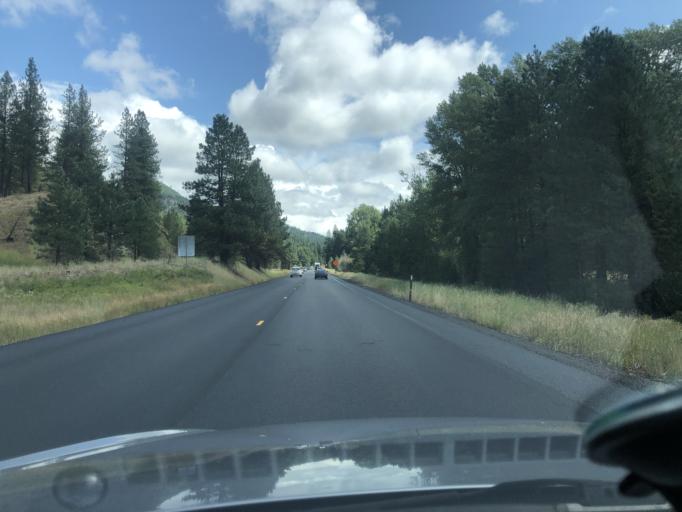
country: US
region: Washington
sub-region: Chelan County
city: Leavenworth
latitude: 47.3239
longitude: -120.6776
